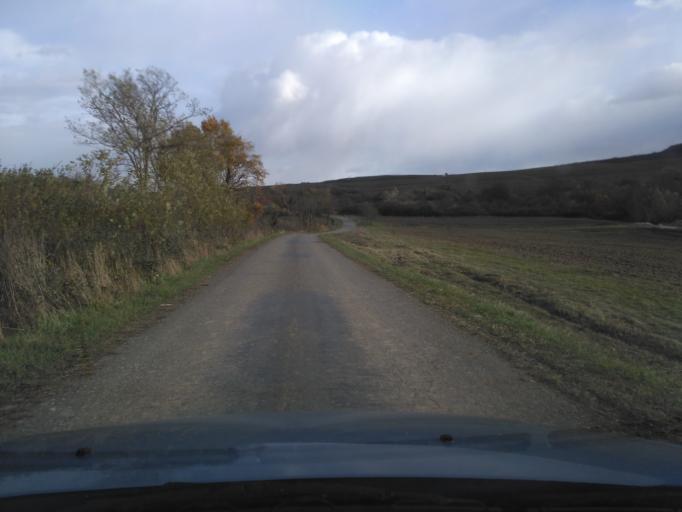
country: HU
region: Borsod-Abauj-Zemplen
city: Satoraljaujhely
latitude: 48.4412
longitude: 21.6997
